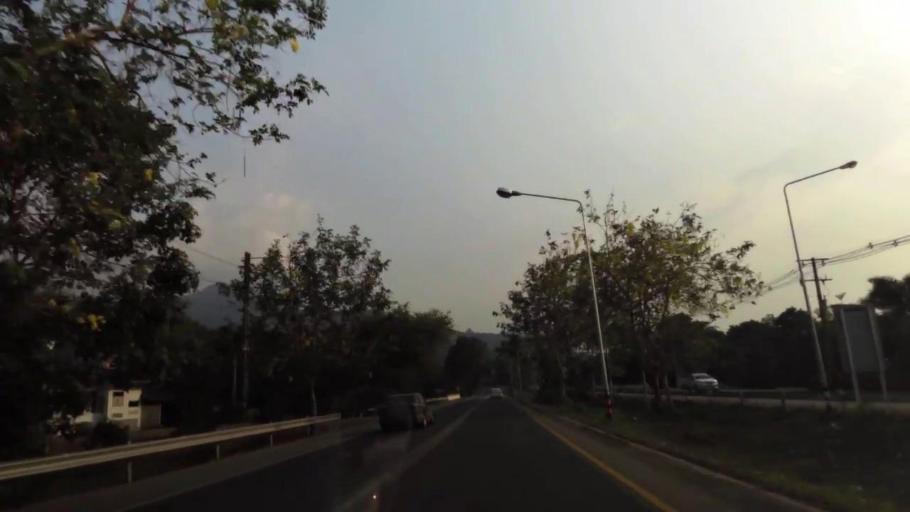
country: TH
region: Chanthaburi
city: Chanthaburi
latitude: 12.5735
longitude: 102.1621
